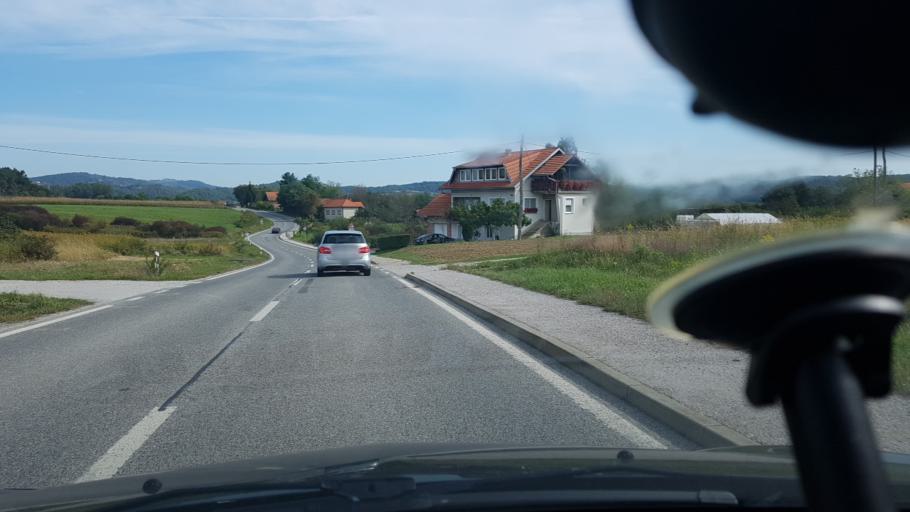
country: HR
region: Krapinsko-Zagorska
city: Marija Bistrica
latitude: 46.0792
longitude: 16.1950
